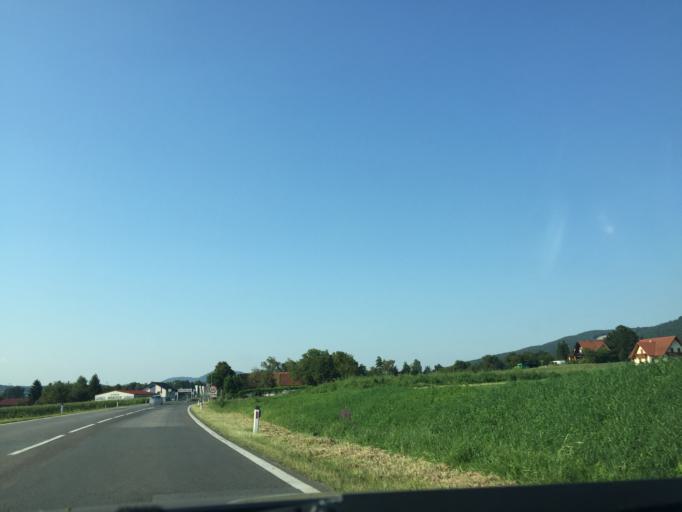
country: AT
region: Styria
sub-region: Politischer Bezirk Suedoststeiermark
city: Stainz bei Straden
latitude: 46.8167
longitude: 15.8935
